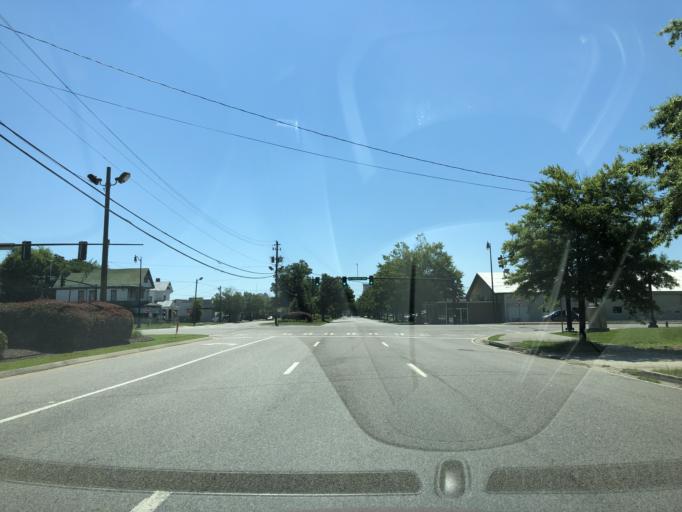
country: US
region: Georgia
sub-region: Richmond County
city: Augusta
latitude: 33.4801
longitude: -81.9801
